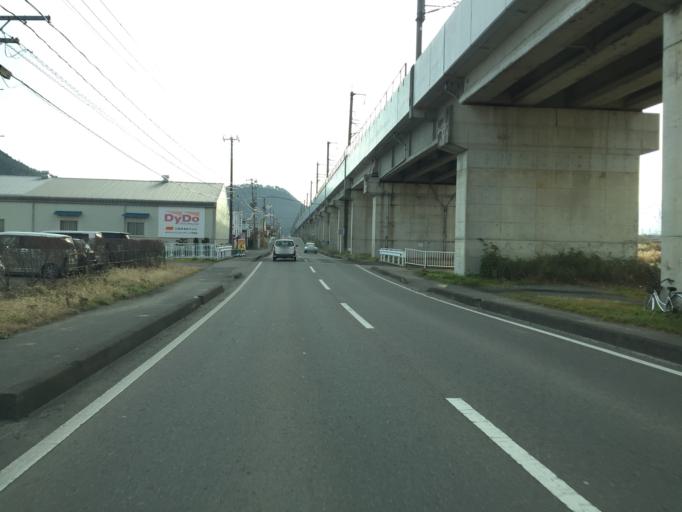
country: JP
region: Fukushima
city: Fukushima-shi
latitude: 37.7890
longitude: 140.4715
